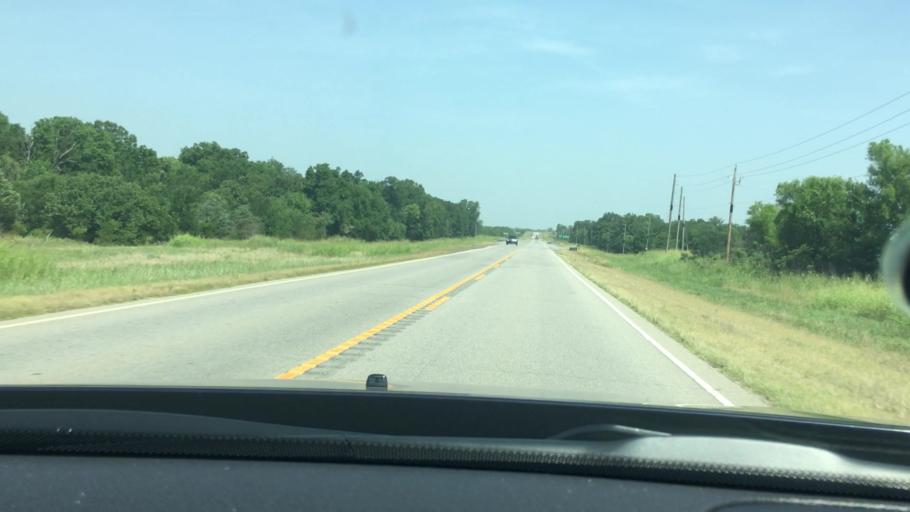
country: US
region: Oklahoma
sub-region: Atoka County
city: Atoka
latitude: 34.4430
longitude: -96.2052
